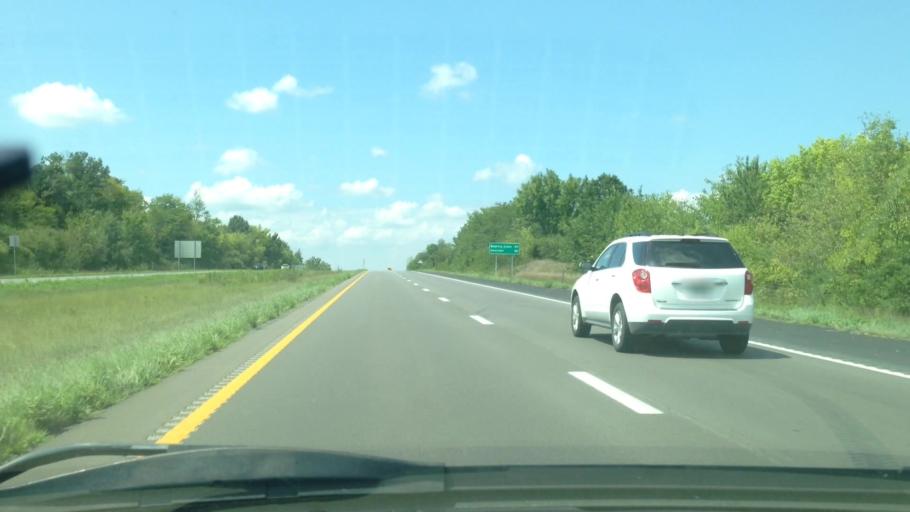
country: US
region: Missouri
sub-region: Lincoln County
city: Troy
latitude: 38.9954
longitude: -90.9684
